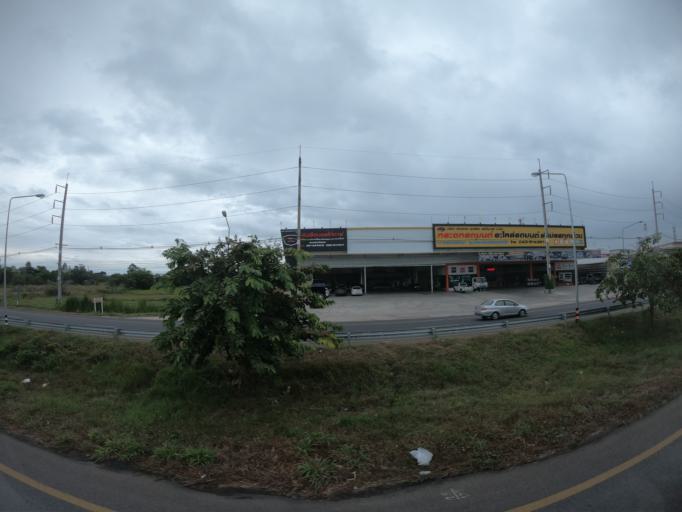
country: TH
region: Roi Et
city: Roi Et
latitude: 16.0506
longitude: 103.6206
